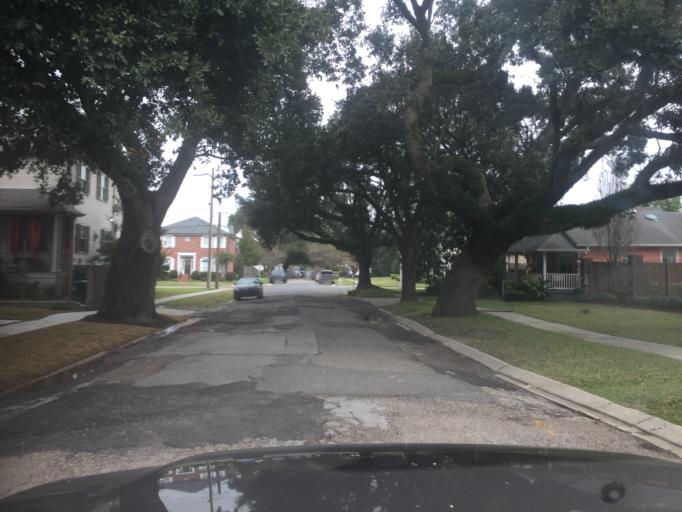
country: US
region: Louisiana
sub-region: Jefferson Parish
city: Metairie
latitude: 30.0003
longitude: -90.1063
